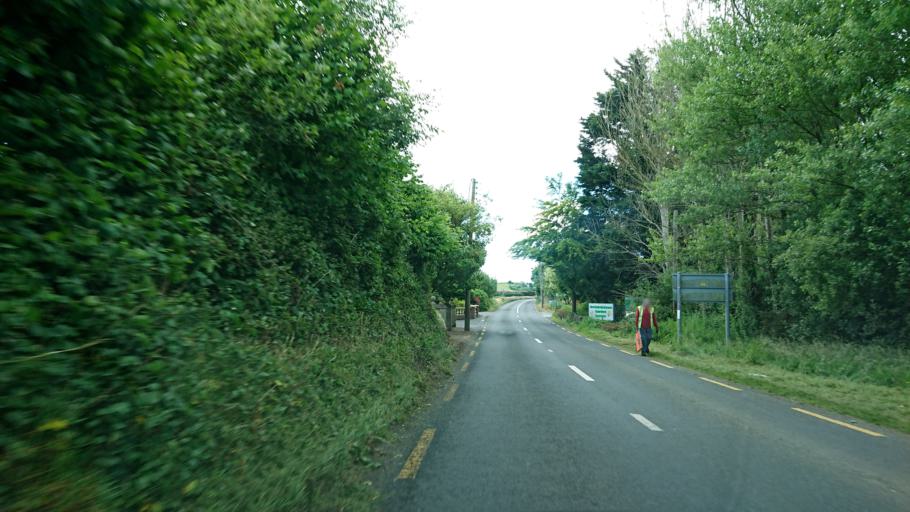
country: IE
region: Leinster
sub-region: Kilkenny
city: Mooncoin
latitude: 52.2306
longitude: -7.2003
